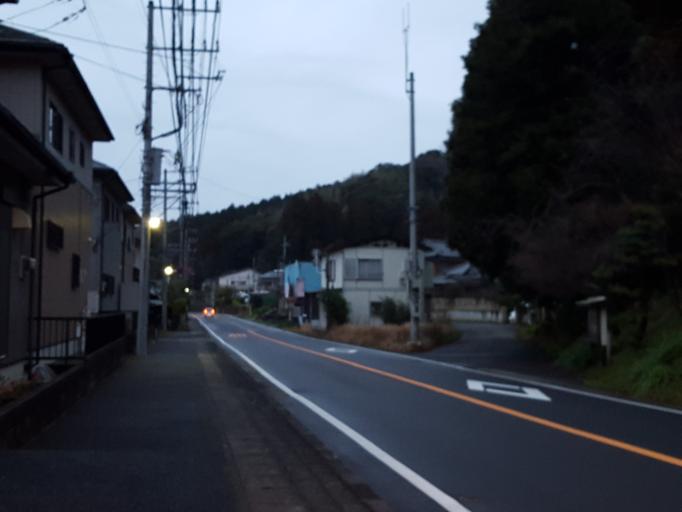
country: JP
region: Chiba
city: Ichihara
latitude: 35.4559
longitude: 140.0542
